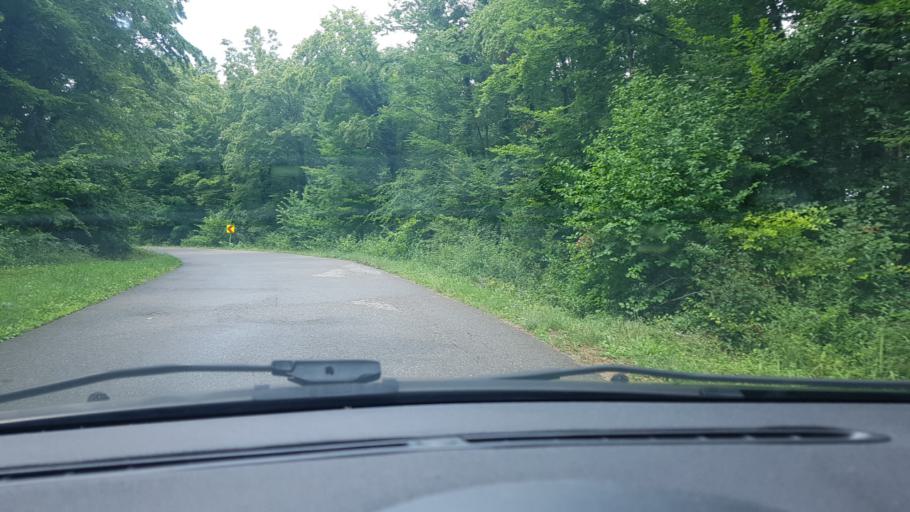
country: BA
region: Federation of Bosnia and Herzegovina
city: Trzacka Rastela
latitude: 44.9771
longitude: 15.7067
